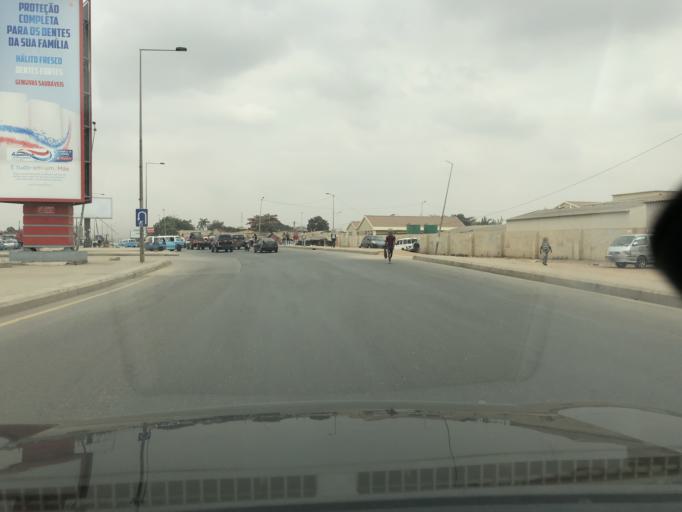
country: AO
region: Luanda
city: Luanda
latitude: -8.8244
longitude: 13.2821
